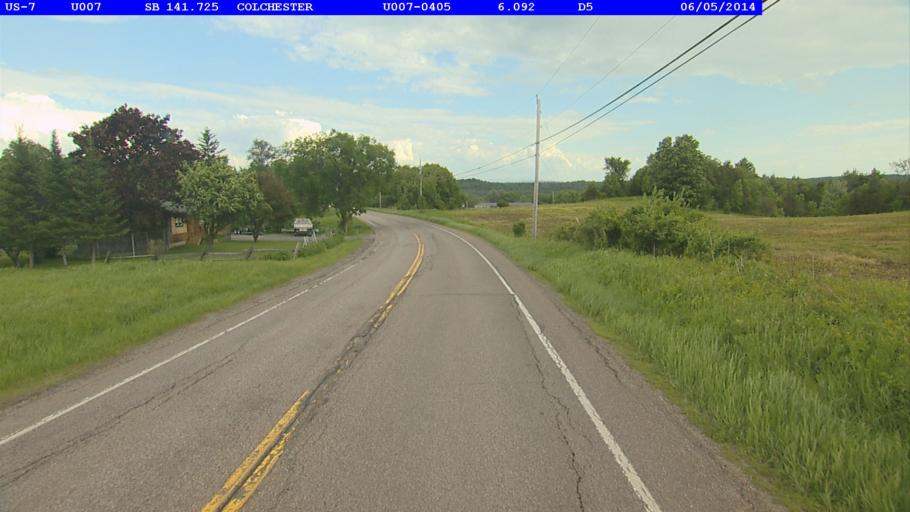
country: US
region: Vermont
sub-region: Chittenden County
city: Colchester
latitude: 44.5836
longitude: -73.1647
